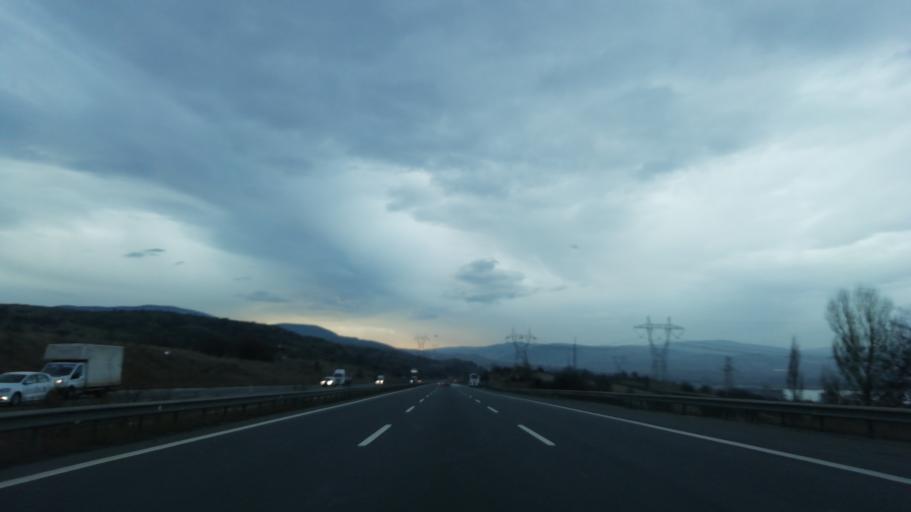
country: TR
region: Bolu
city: Yenicaga
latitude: 40.7650
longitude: 32.0502
